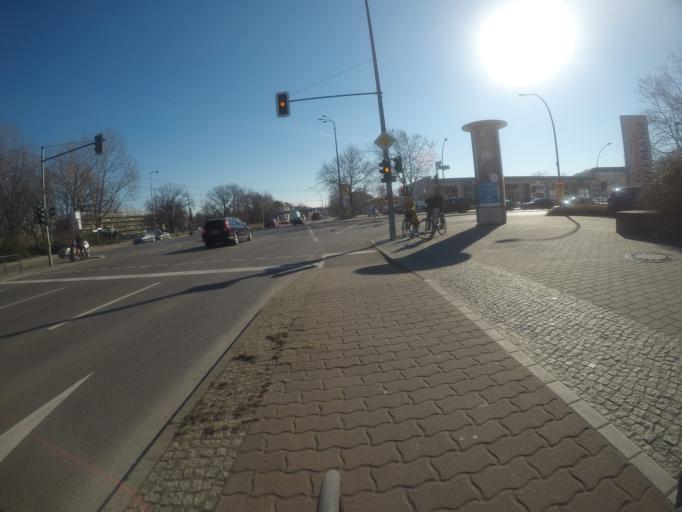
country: DE
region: Berlin
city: Karlshorst
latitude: 52.4961
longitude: 13.5242
